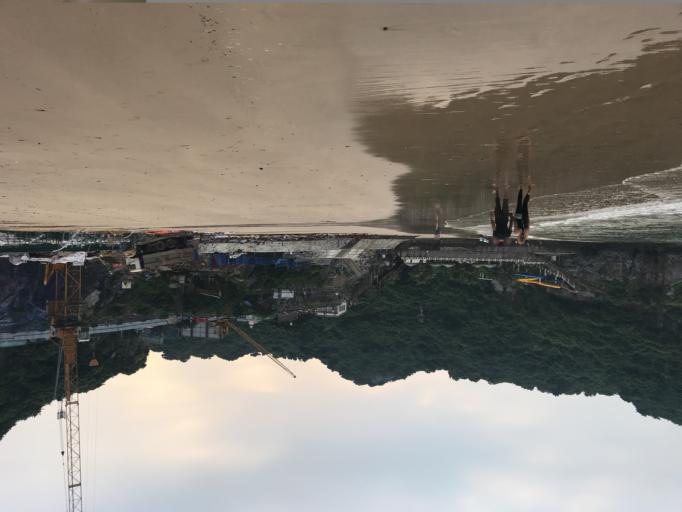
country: VN
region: Hai Phong
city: Cat Ba
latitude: 20.7181
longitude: 107.0535
